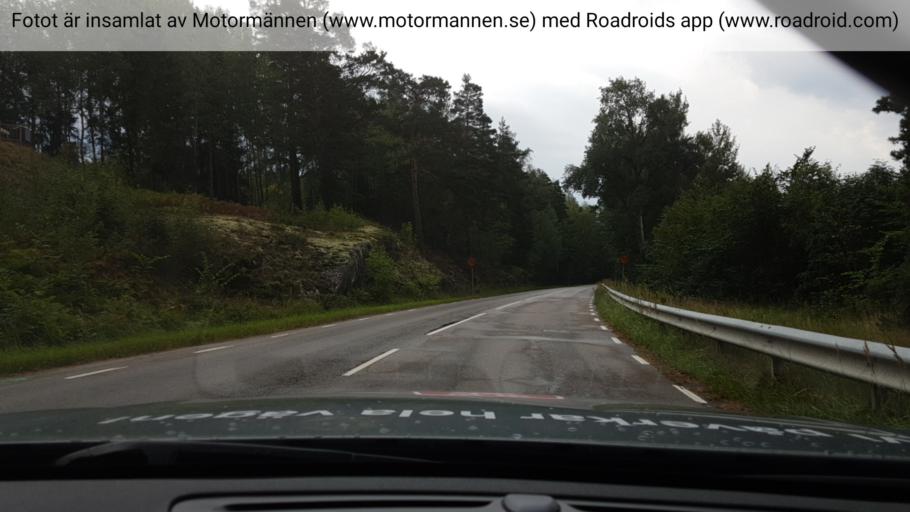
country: SE
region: Uppsala
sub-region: Habo Kommun
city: Balsta
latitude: 59.5499
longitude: 17.5586
